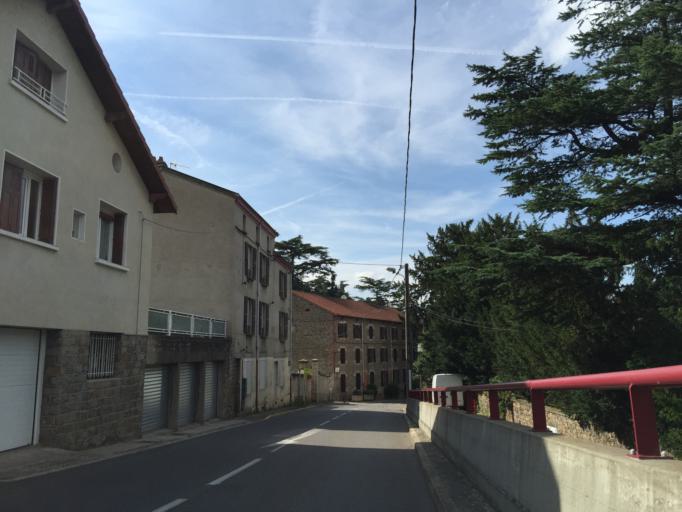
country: FR
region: Rhone-Alpes
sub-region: Departement de la Loire
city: Saint-Chamond
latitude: 45.4516
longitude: 4.5040
